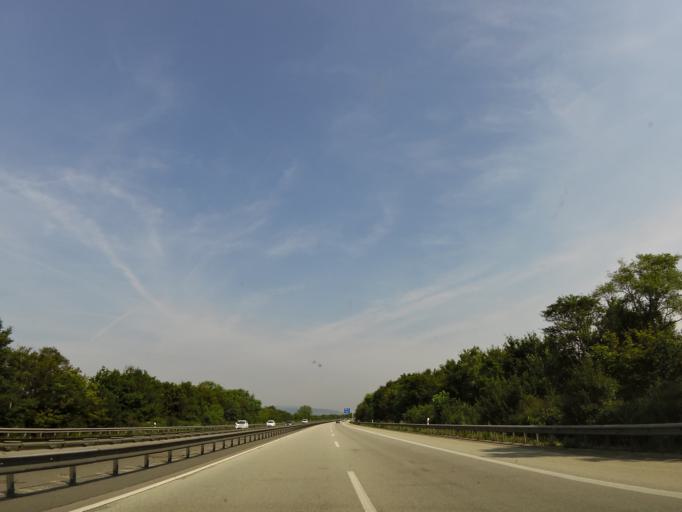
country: DE
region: Rheinland-Pfalz
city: Welgesheim
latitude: 49.8807
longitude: 7.9508
